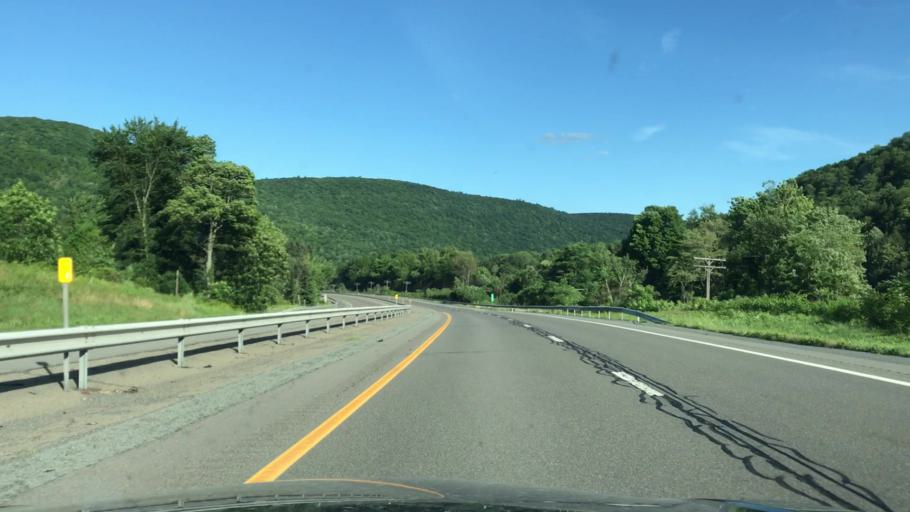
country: US
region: New York
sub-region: Delaware County
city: Hancock
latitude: 41.9991
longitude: -75.3539
